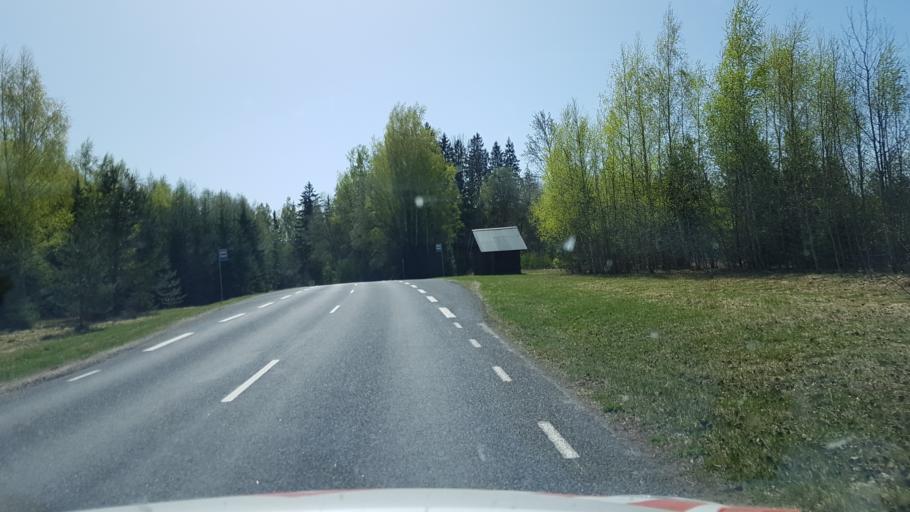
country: EE
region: Viljandimaa
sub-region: Suure-Jaani vald
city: Suure-Jaani
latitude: 58.4749
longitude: 25.4438
